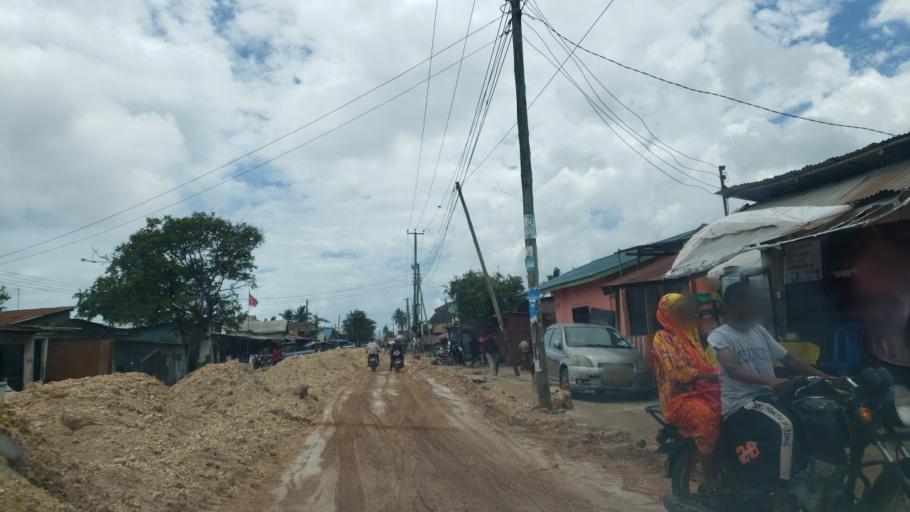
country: TZ
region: Dar es Salaam
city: Magomeni
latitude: -6.8062
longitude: 39.2276
